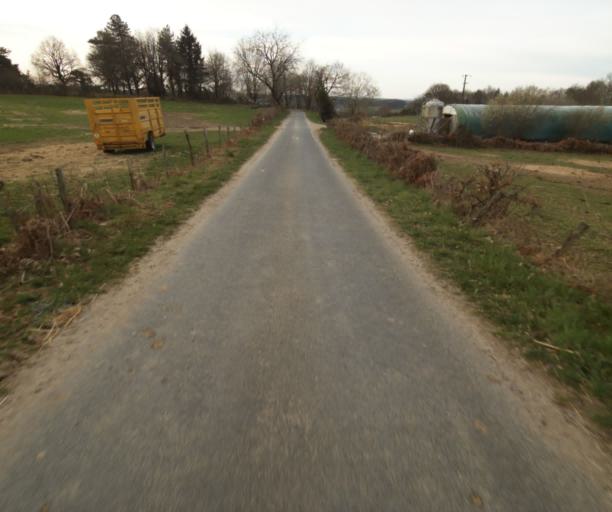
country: FR
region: Limousin
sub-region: Departement de la Correze
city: Correze
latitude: 45.4394
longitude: 1.8227
